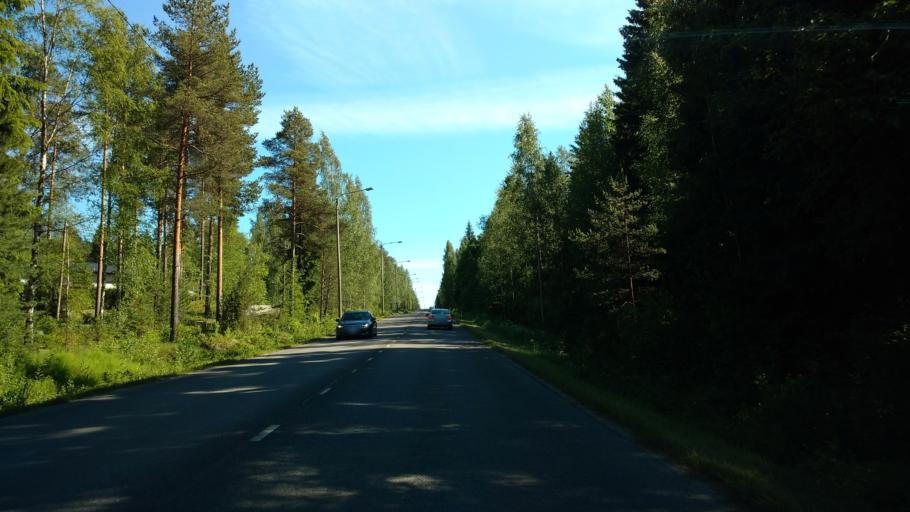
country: FI
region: Varsinais-Suomi
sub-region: Salo
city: Salo
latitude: 60.3973
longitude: 23.1771
